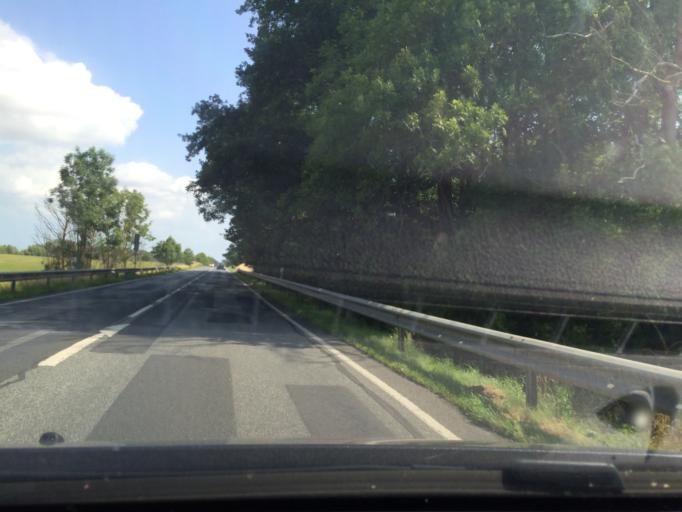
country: DE
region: Mecklenburg-Vorpommern
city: Sehlen
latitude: 54.3853
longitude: 13.3590
